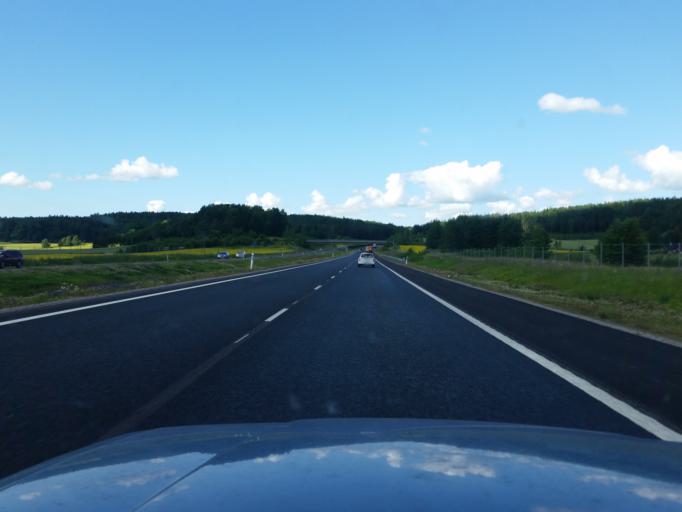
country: FI
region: Varsinais-Suomi
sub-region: Salo
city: Muurla
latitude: 60.3895
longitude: 23.2886
